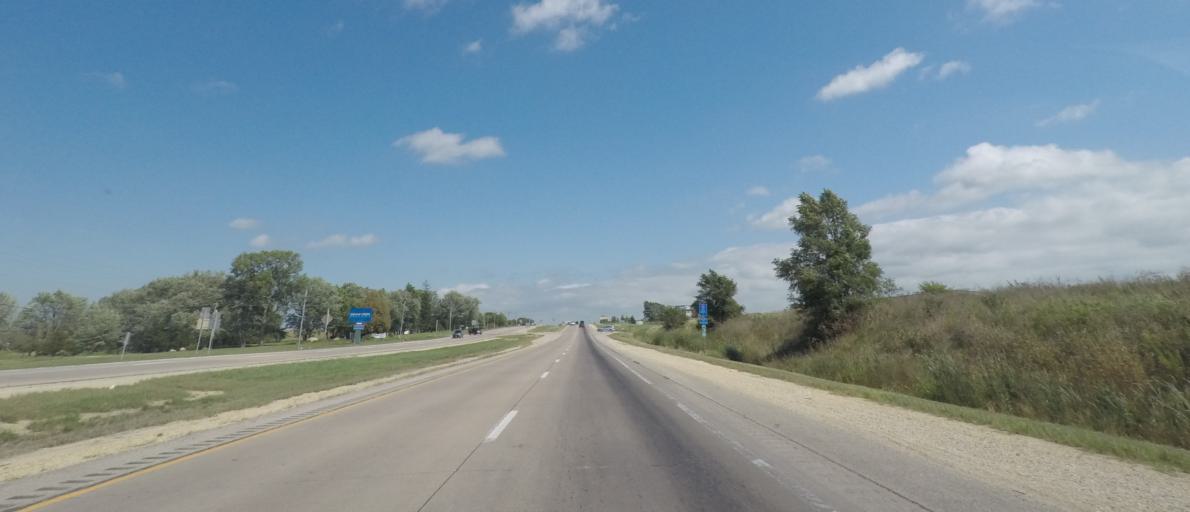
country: US
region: Iowa
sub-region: Linn County
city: Marion
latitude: 42.0356
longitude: -91.5474
